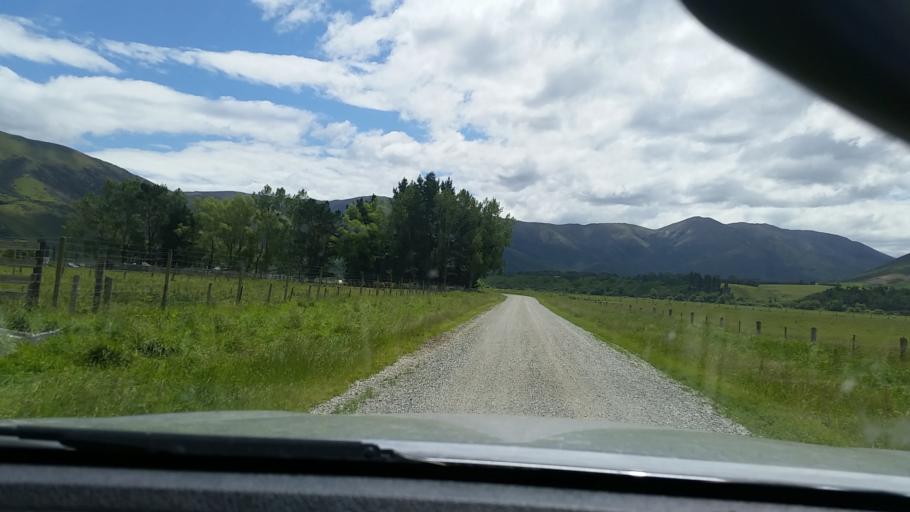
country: NZ
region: Otago
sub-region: Queenstown-Lakes District
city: Kingston
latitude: -45.6989
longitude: 168.6565
